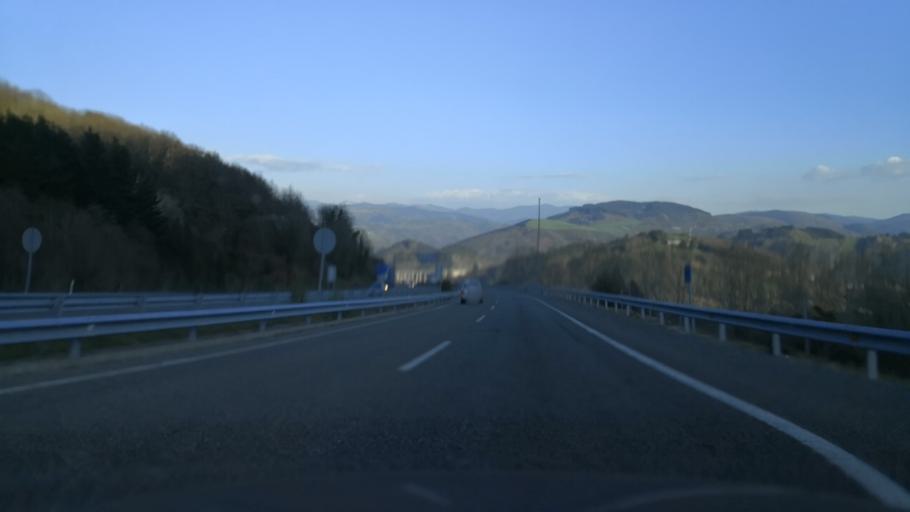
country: ES
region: Galicia
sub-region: Provincia de Lugo
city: Becerrea
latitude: 42.8652
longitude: -7.1639
